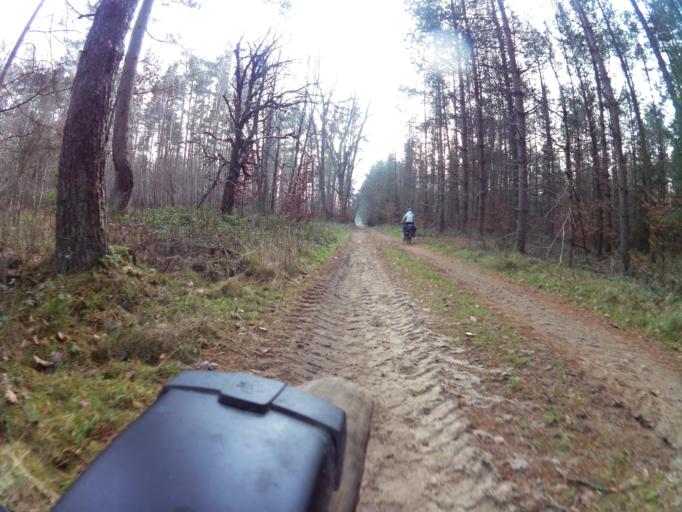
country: PL
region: West Pomeranian Voivodeship
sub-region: Powiat koszalinski
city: Polanow
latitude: 54.1480
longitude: 16.7303
